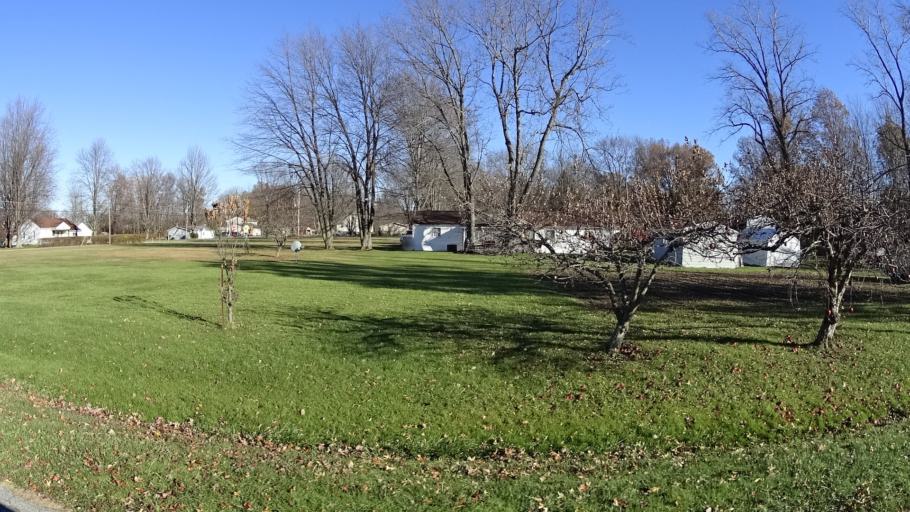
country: US
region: Ohio
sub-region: Lorain County
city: Elyria
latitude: 41.3305
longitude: -82.1364
